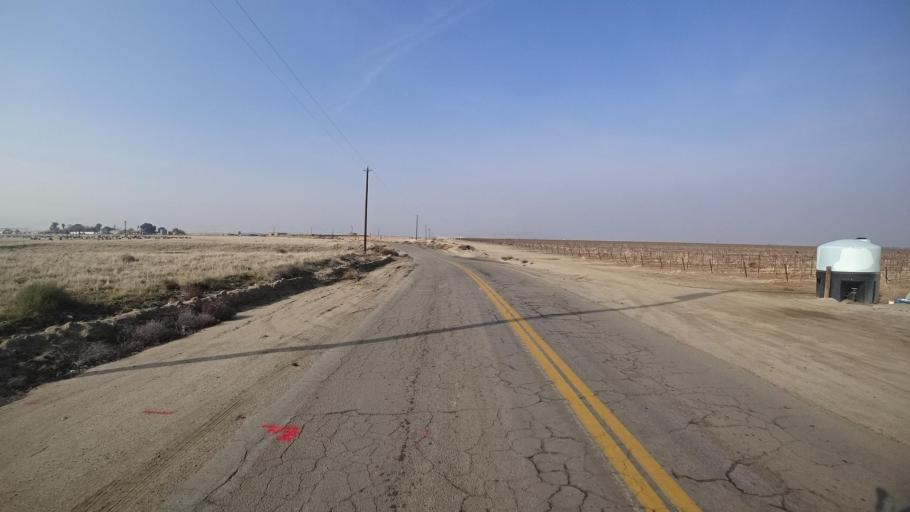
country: US
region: California
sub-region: Kern County
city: Lebec
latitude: 34.9931
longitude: -118.9045
